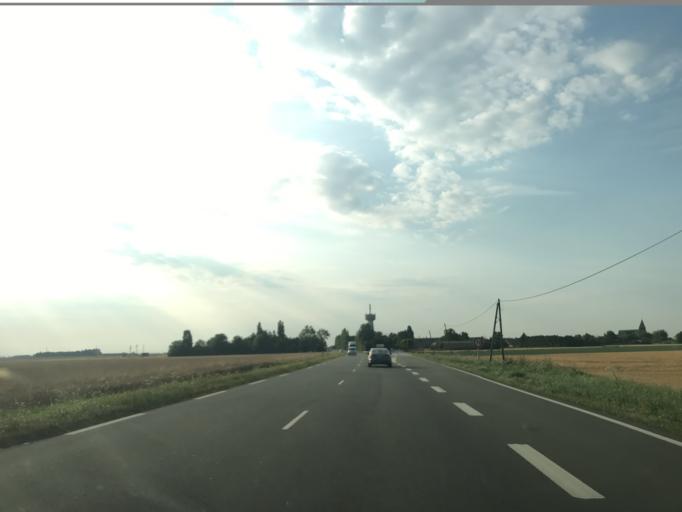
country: FR
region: Ile-de-France
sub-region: Departement des Yvelines
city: Ablis
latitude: 48.4674
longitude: 1.8723
